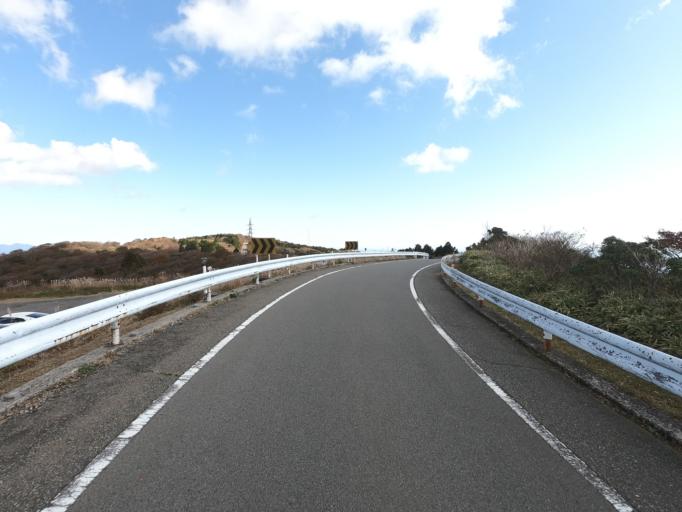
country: JP
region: Kanagawa
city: Hakone
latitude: 35.1852
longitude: 139.0492
